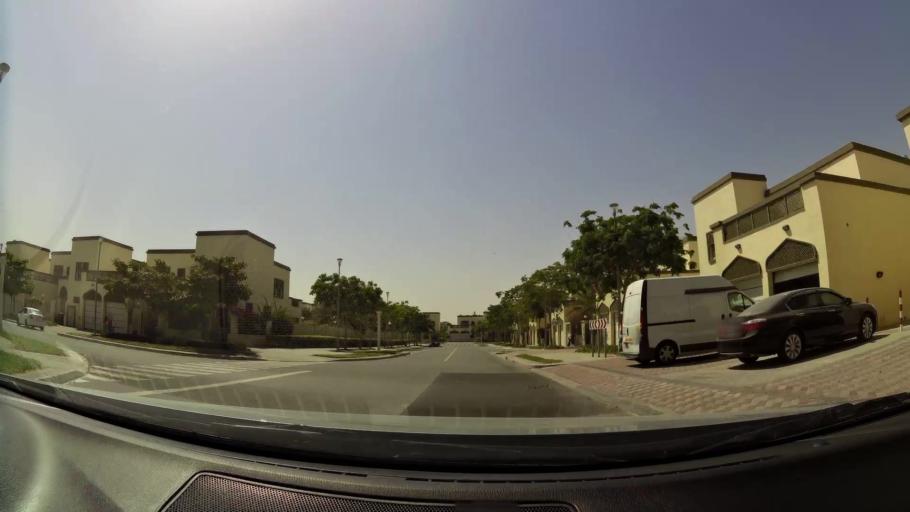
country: AE
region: Dubai
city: Dubai
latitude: 25.0489
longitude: 55.1473
